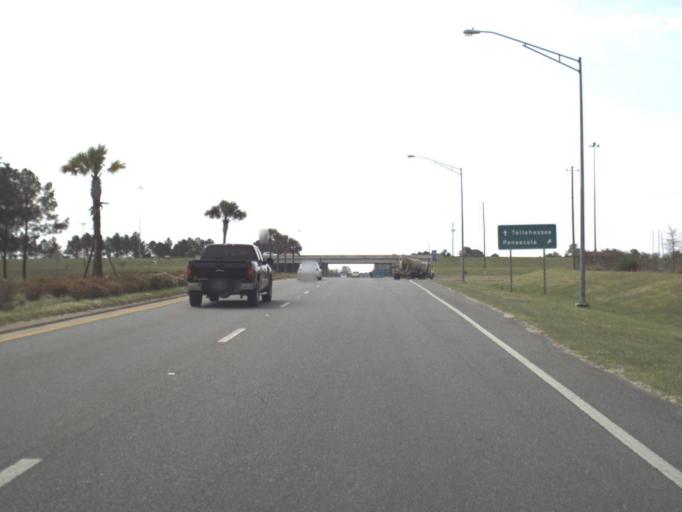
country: US
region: Florida
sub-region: Holmes County
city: Bonifay
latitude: 30.7654
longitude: -85.6849
